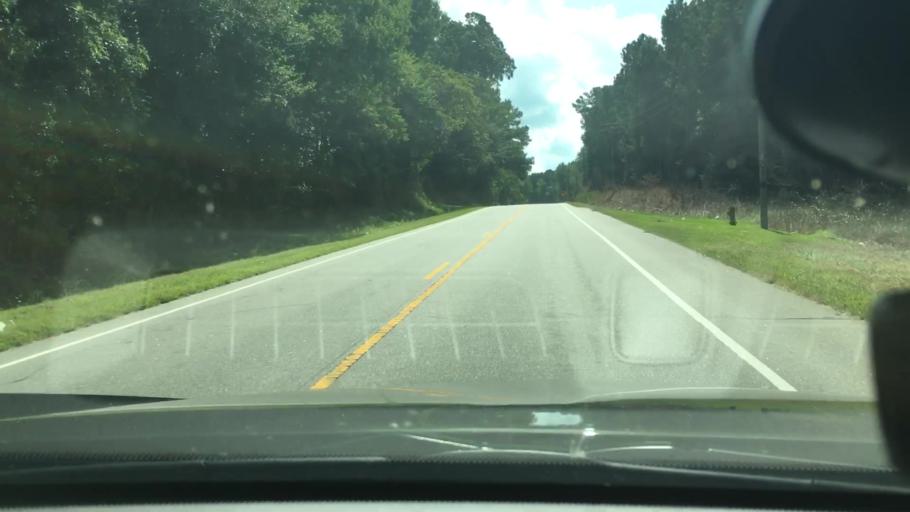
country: US
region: North Carolina
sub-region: Edgecombe County
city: Pinetops
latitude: 35.7844
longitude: -77.6184
